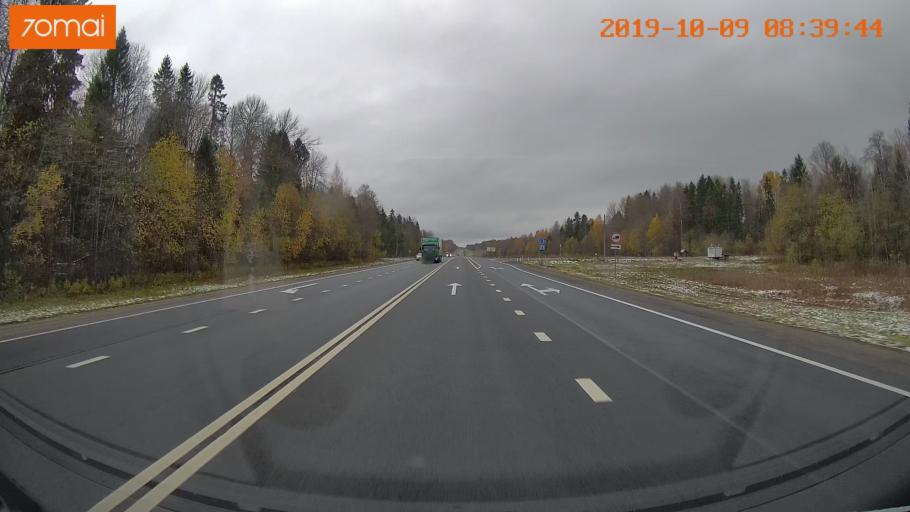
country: RU
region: Vologda
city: Gryazovets
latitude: 58.9759
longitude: 40.1494
